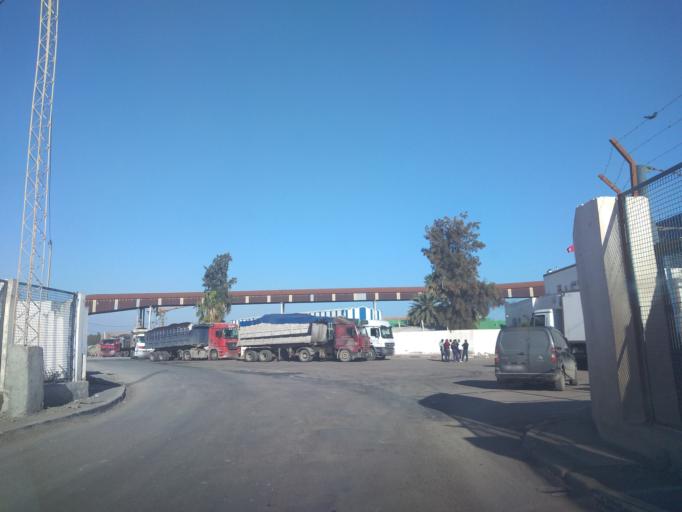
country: TN
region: Safaqis
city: Sfax
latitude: 34.7318
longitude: 10.7686
